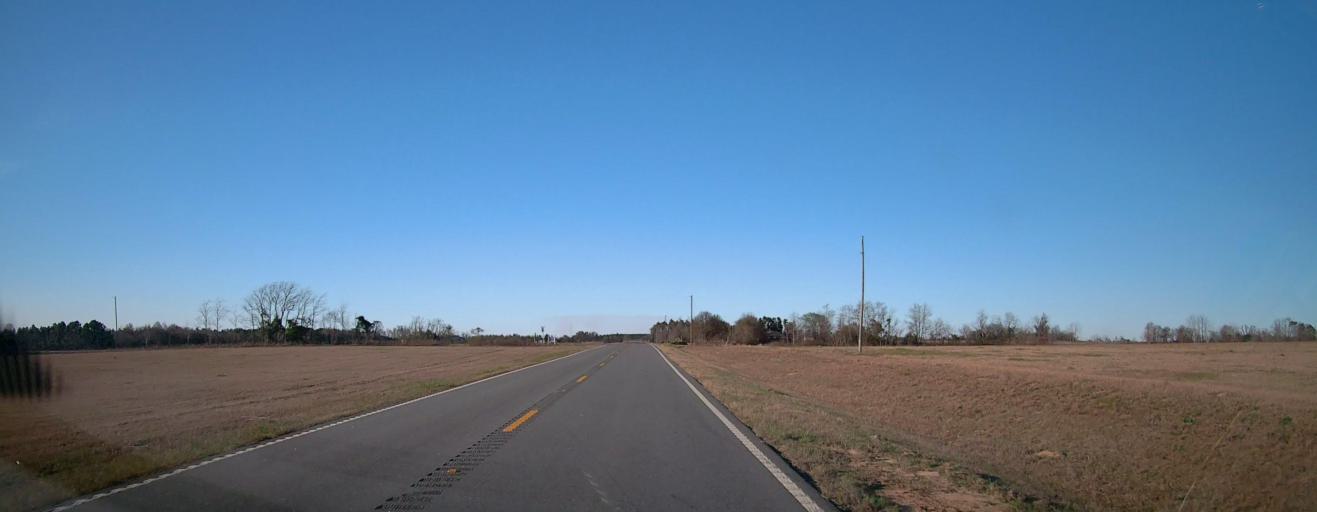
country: US
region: Georgia
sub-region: Talbot County
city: Talbotton
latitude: 32.5380
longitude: -84.4350
